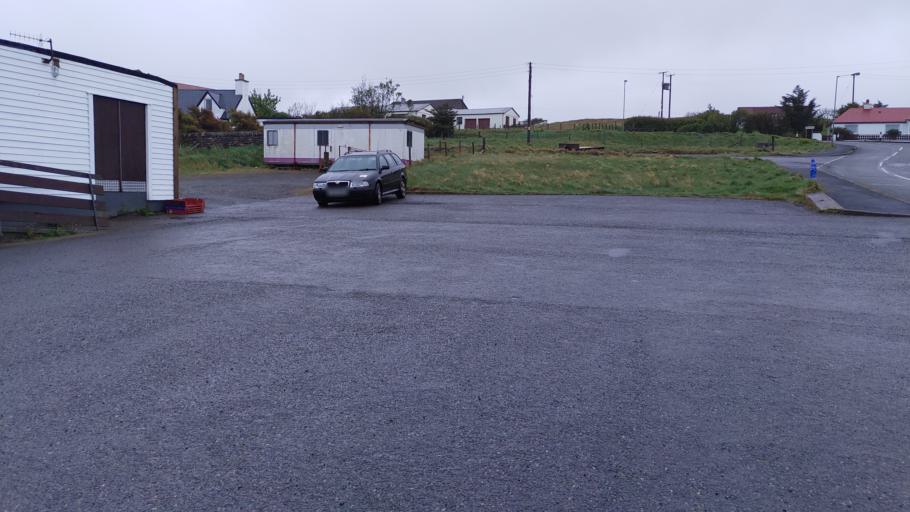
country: GB
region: Scotland
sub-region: Shetland Islands
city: Shetland
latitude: 60.5986
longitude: -1.0726
